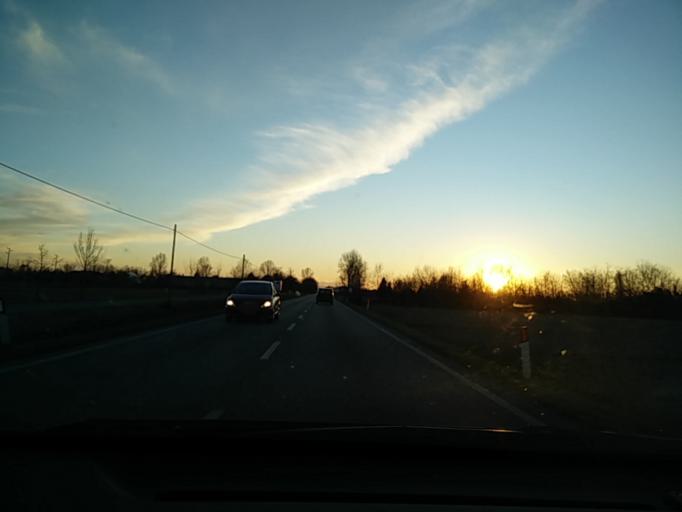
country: IT
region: Veneto
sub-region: Provincia di Venezia
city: Teglio Veneto
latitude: 45.8298
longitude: 12.8890
